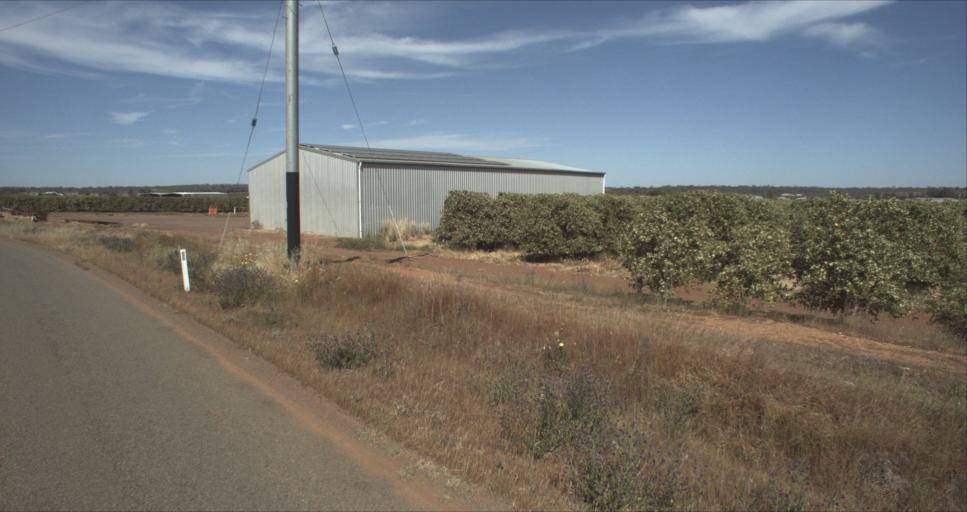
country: AU
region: New South Wales
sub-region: Leeton
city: Leeton
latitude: -34.5826
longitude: 146.4767
